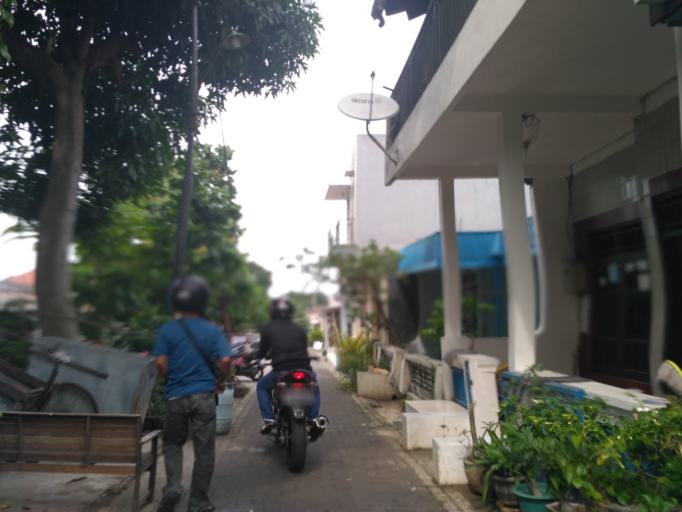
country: ID
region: Central Java
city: Ungaran
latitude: -7.0723
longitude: 110.4294
